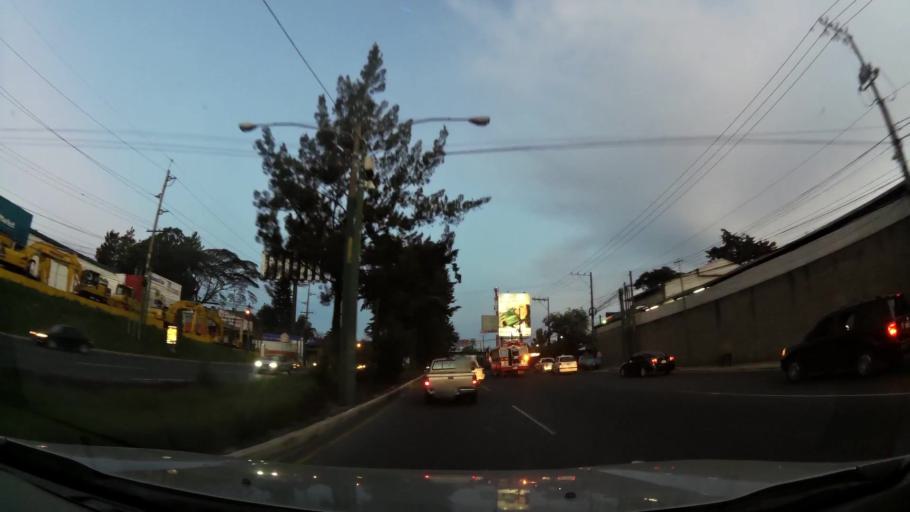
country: GT
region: Guatemala
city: Mixco
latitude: 14.6350
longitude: -90.5970
